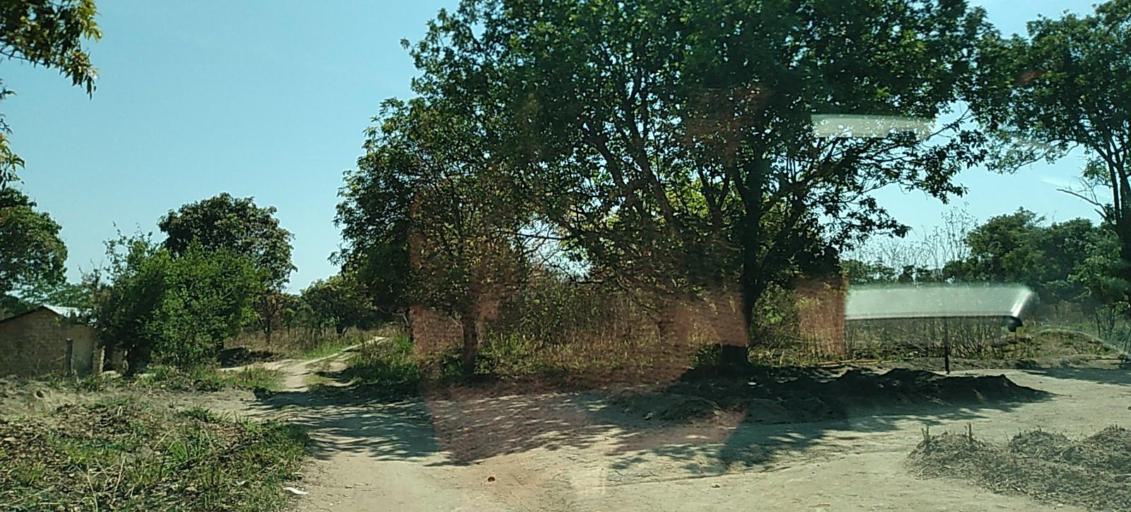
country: ZM
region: Copperbelt
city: Chililabombwe
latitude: -12.2867
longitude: 27.8805
